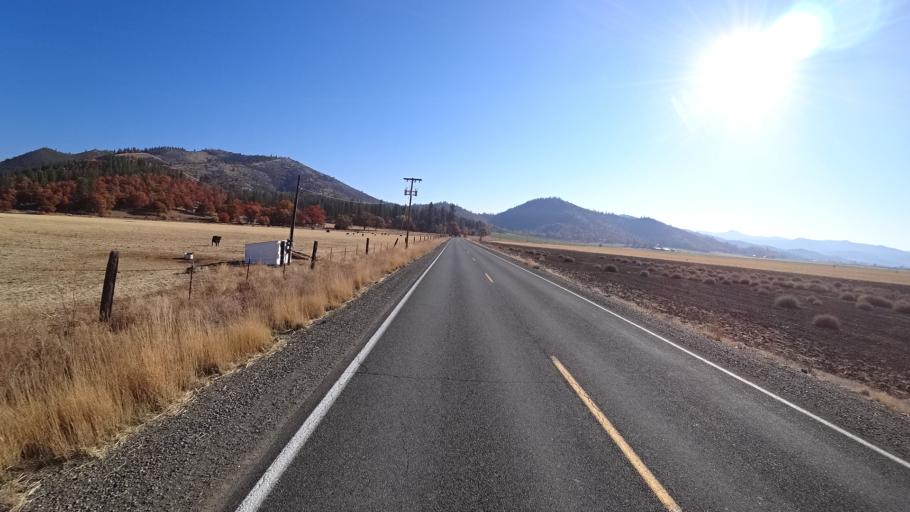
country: US
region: California
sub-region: Siskiyou County
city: Yreka
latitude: 41.6287
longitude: -122.8767
